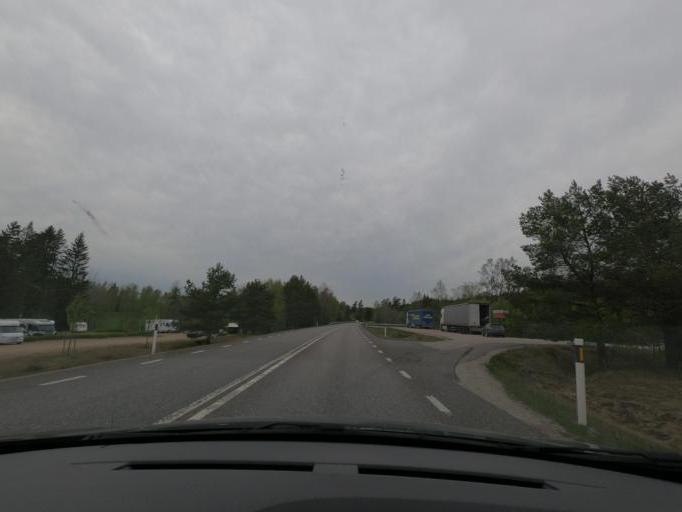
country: SE
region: Vaestra Goetaland
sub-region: Tranemo Kommun
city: Tranemo
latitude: 57.4722
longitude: 13.3759
